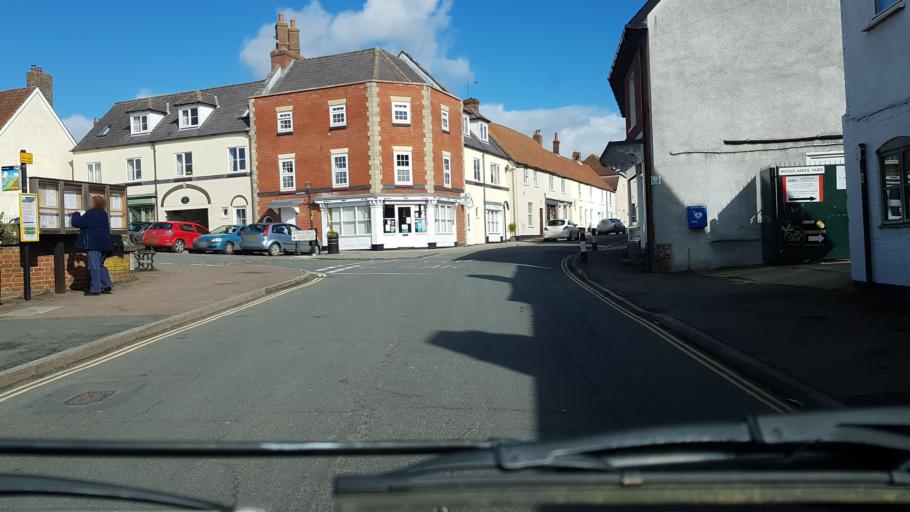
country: GB
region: England
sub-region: Wiltshire
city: Market Lavington
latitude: 51.2869
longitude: -1.9787
